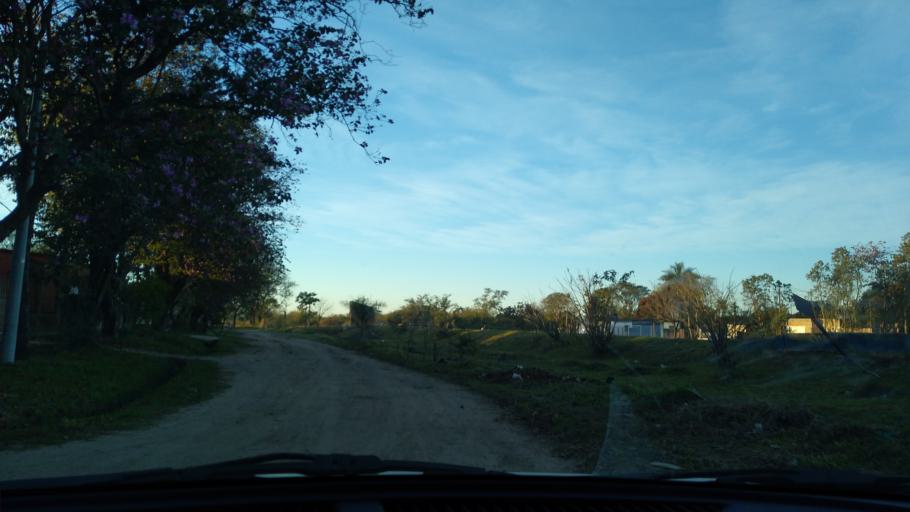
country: AR
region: Chaco
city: Barranqueras
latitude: -27.4796
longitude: -58.9629
